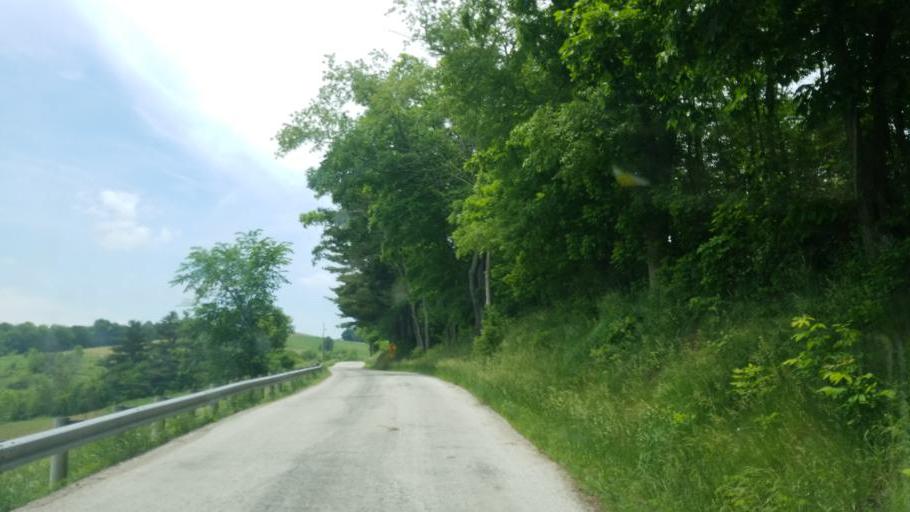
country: US
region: Ohio
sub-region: Coshocton County
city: West Lafayette
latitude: 40.3773
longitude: -81.7707
